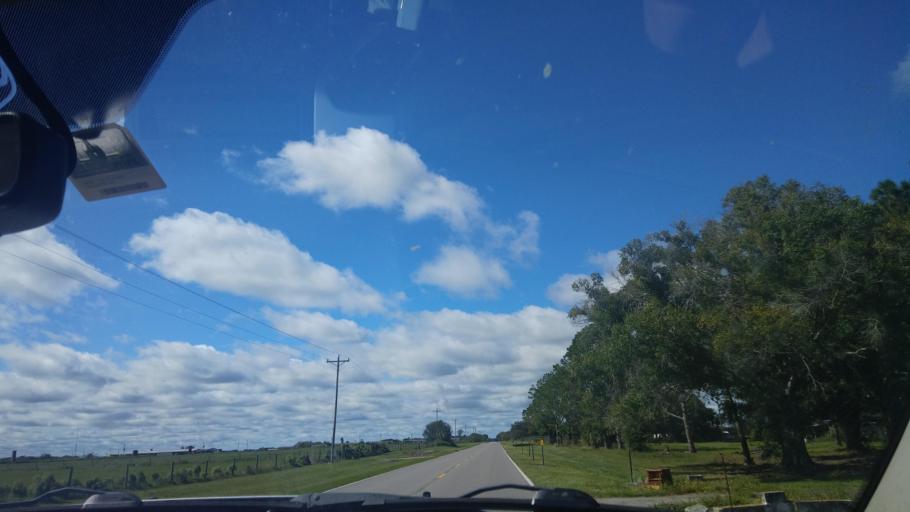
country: US
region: Florida
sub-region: Okeechobee County
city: Cypress Quarters
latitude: 27.3905
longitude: -80.8202
